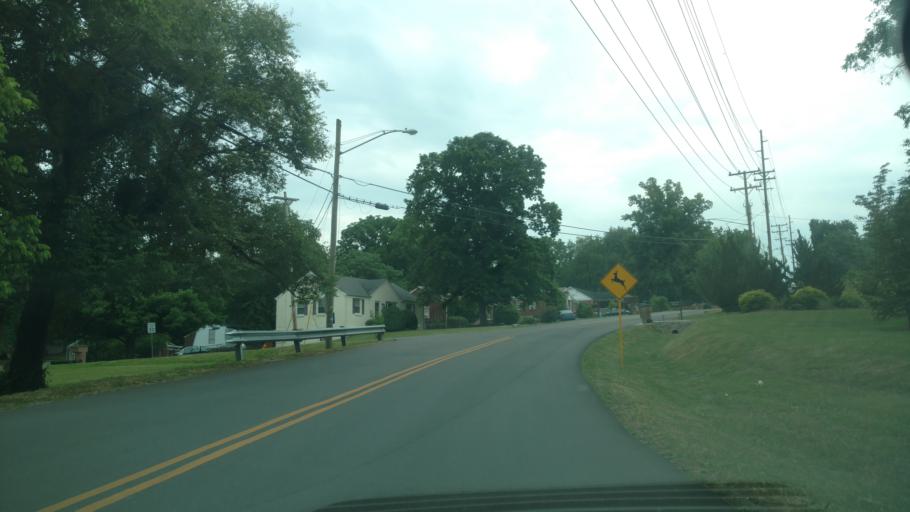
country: US
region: Tennessee
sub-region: Davidson County
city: Nashville
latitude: 36.1953
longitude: -86.7087
